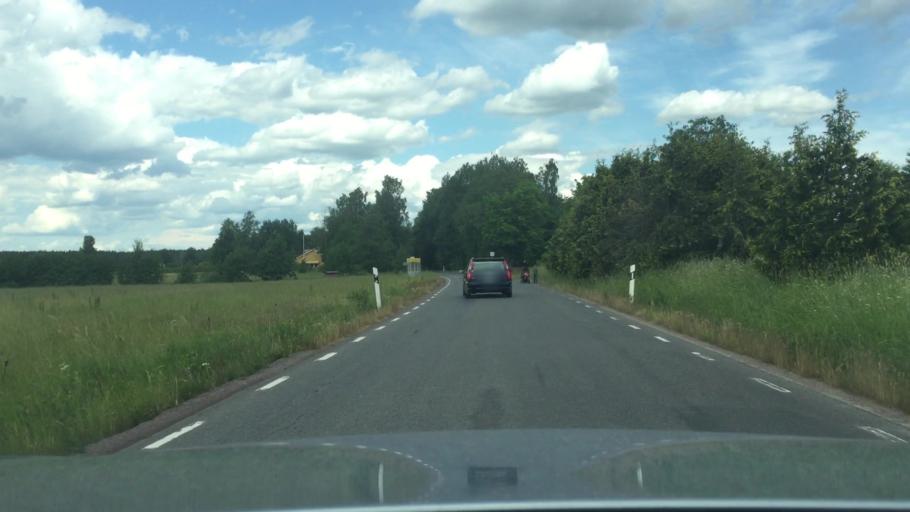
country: SE
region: Vaestra Goetaland
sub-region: Tidaholms Kommun
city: Tidaholm
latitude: 58.1937
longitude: 13.9774
